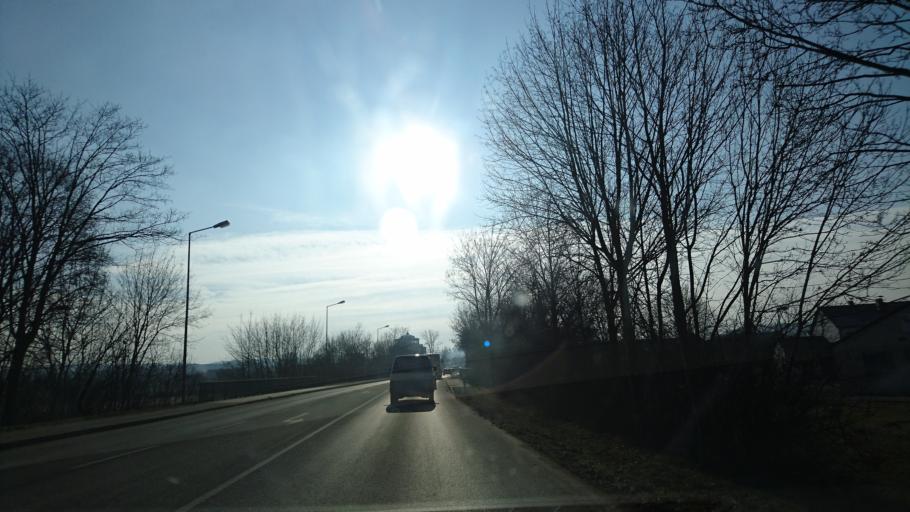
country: DE
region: Bavaria
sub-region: Lower Bavaria
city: Pfarrkirchen
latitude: 48.4269
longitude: 12.9431
